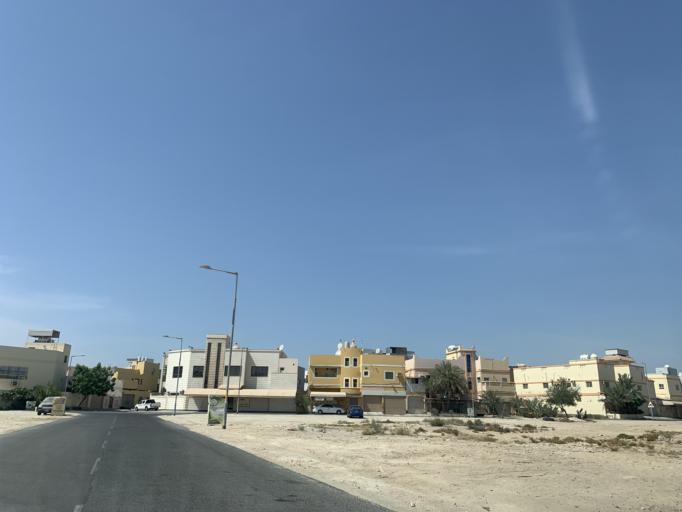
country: BH
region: Central Governorate
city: Madinat Hamad
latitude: 26.1806
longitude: 50.4745
